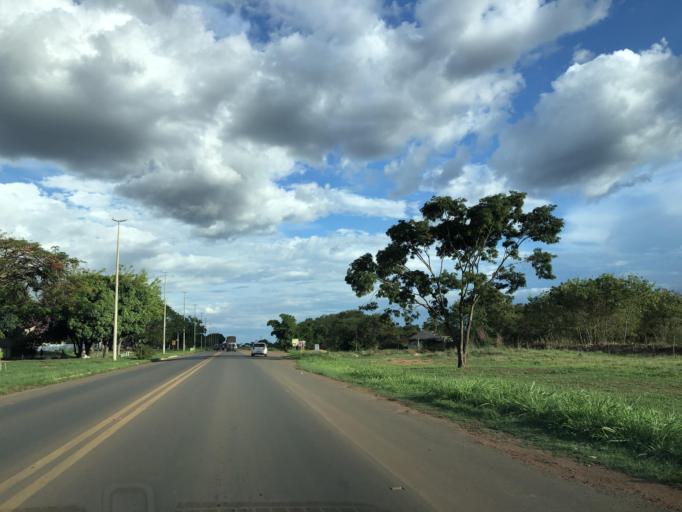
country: BR
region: Goias
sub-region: Luziania
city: Luziania
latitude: -16.0330
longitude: -48.0749
